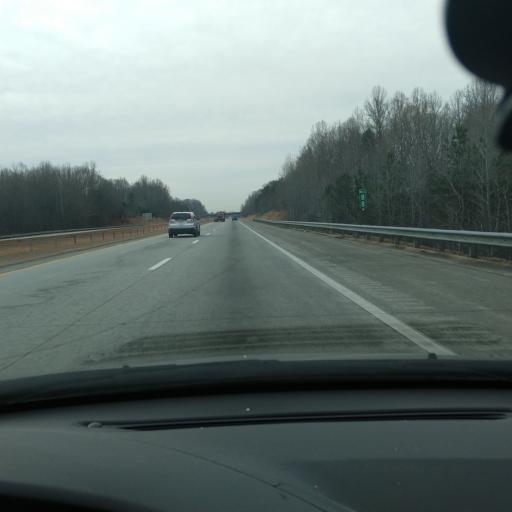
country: US
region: North Carolina
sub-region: Davidson County
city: Lexington
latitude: 35.8247
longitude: -80.2841
